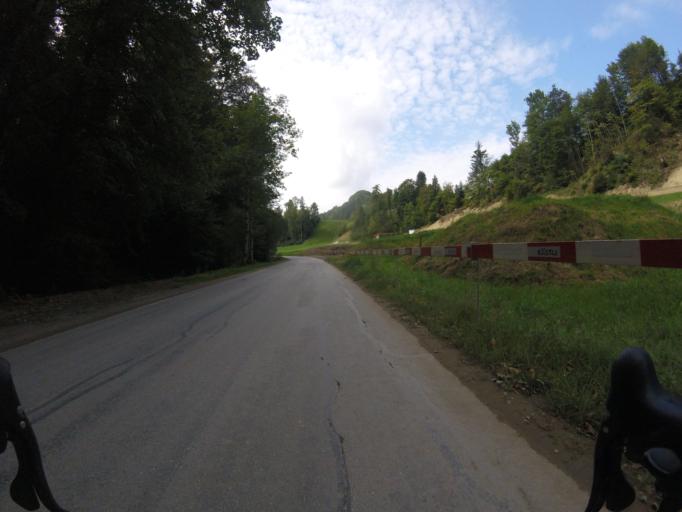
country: CH
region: Bern
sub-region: Emmental District
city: Oberburg
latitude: 47.0289
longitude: 7.6076
